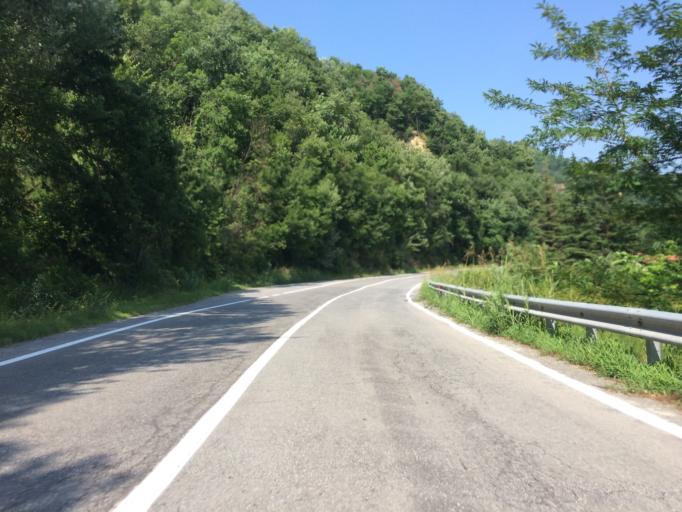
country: IT
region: Piedmont
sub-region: Provincia di Cuneo
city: Torre Bormida
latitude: 44.5823
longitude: 8.1680
